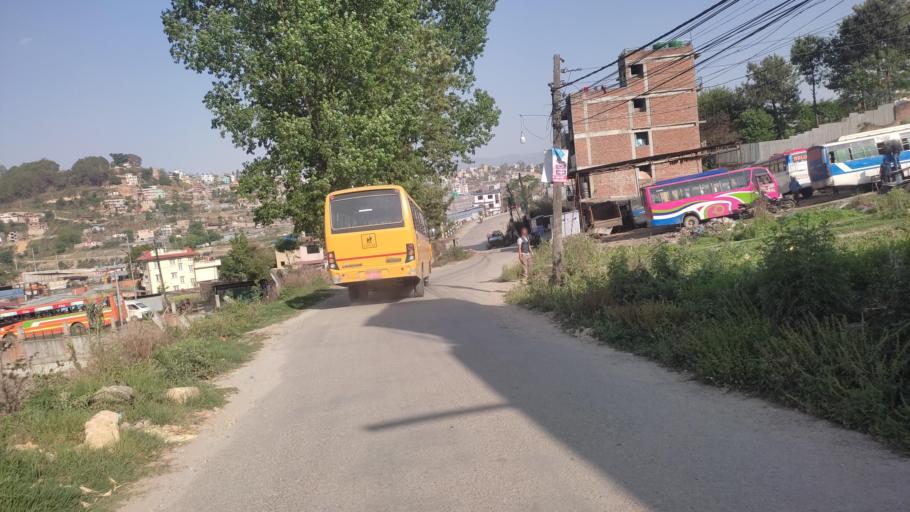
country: NP
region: Central Region
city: Kirtipur
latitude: 27.6540
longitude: 85.2861
